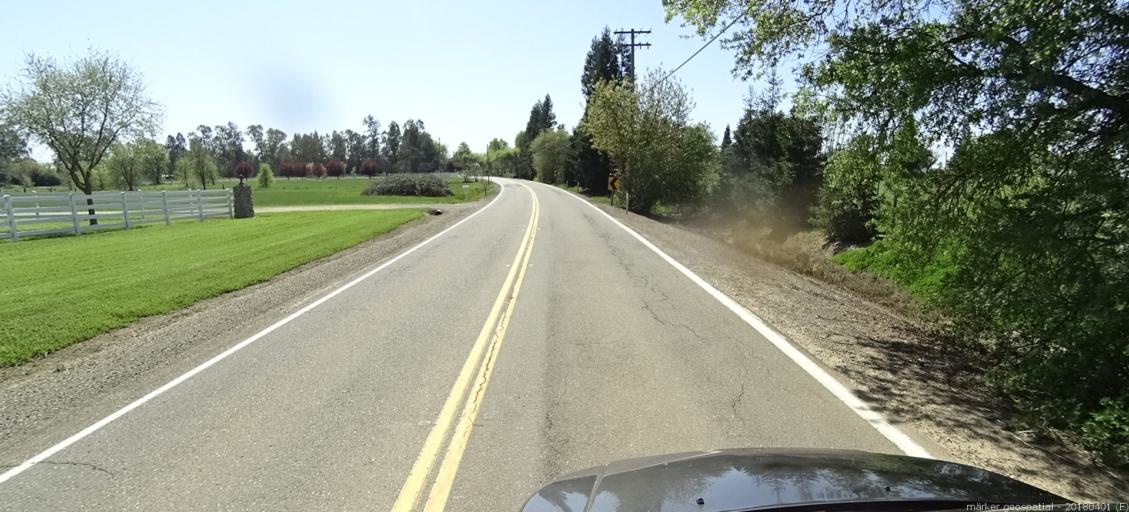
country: US
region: California
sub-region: Sacramento County
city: Wilton
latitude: 38.4181
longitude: -121.2516
